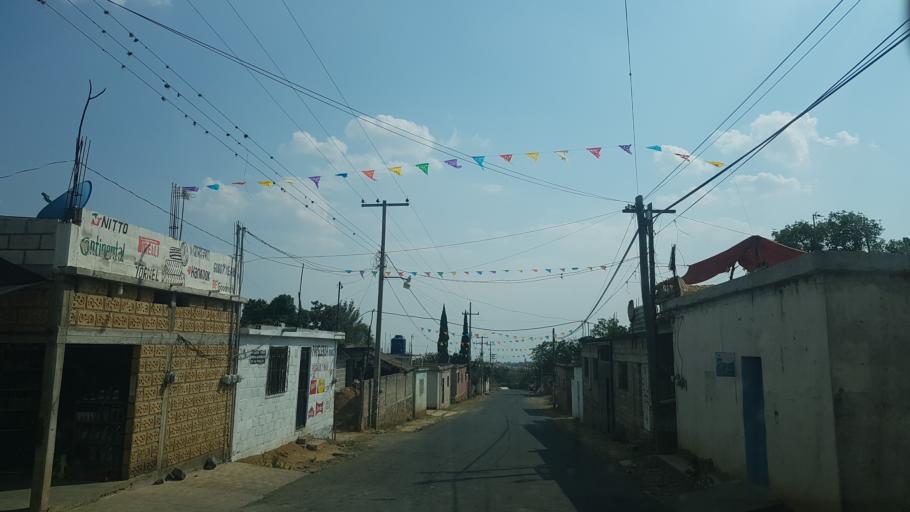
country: MX
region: Puebla
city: San Juan Amecac
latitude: 18.8326
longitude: -98.7035
